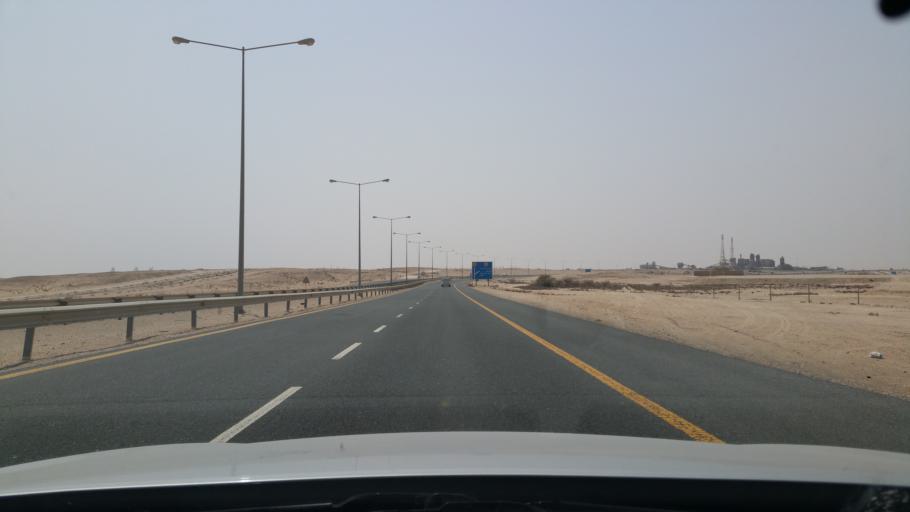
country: QA
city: Umm Bab
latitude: 25.2248
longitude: 50.8054
